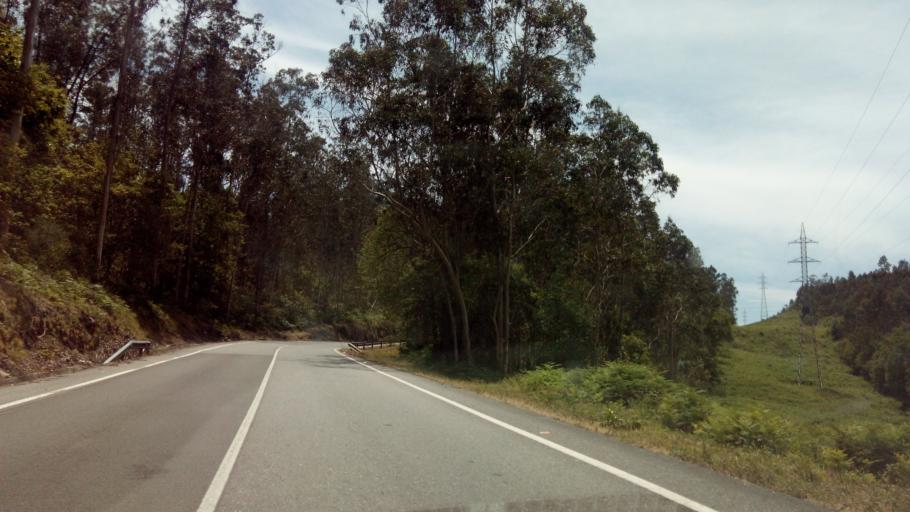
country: ES
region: Galicia
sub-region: Provincia de Pontevedra
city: Marin
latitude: 42.3348
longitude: -8.7140
